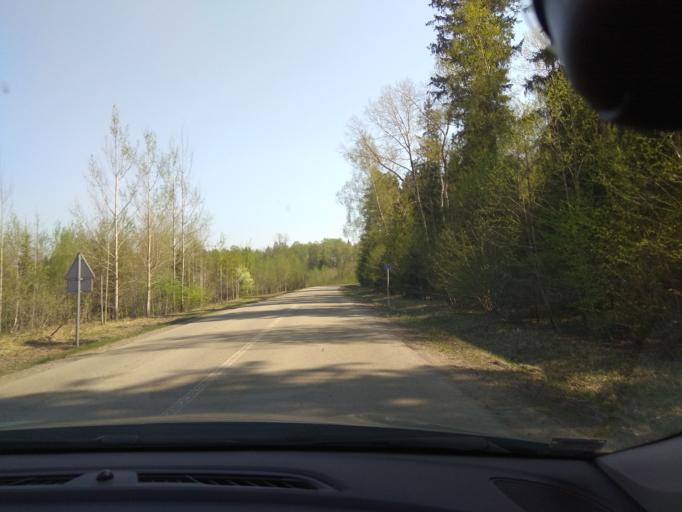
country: LT
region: Panevezys
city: Pasvalys
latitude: 55.9810
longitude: 24.1828
